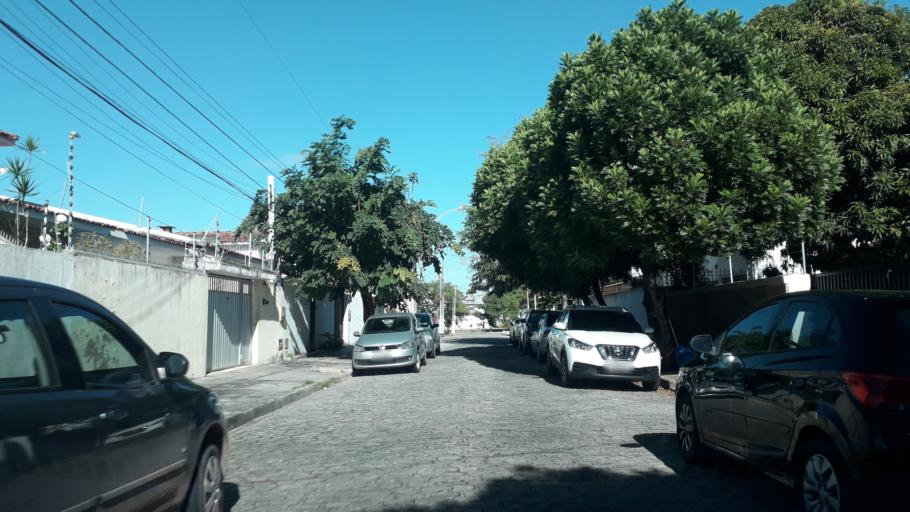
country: BR
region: Alagoas
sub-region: Maceio
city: Maceio
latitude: -9.6676
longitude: -35.7312
